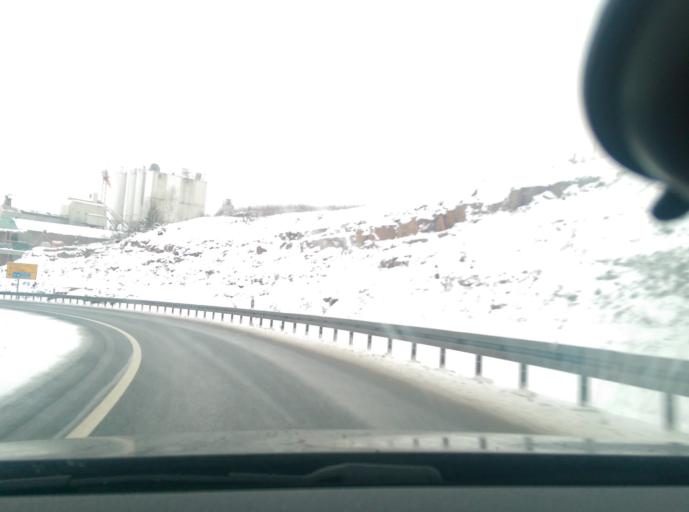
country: DE
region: Hesse
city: Hessisch Lichtenau
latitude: 51.2117
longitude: 9.7195
